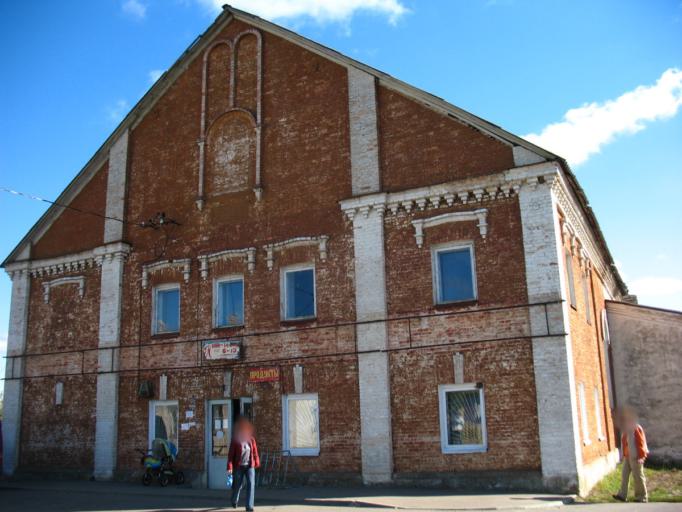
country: BY
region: Grodnenskaya
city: Shchuchin
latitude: 53.8144
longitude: 24.5604
